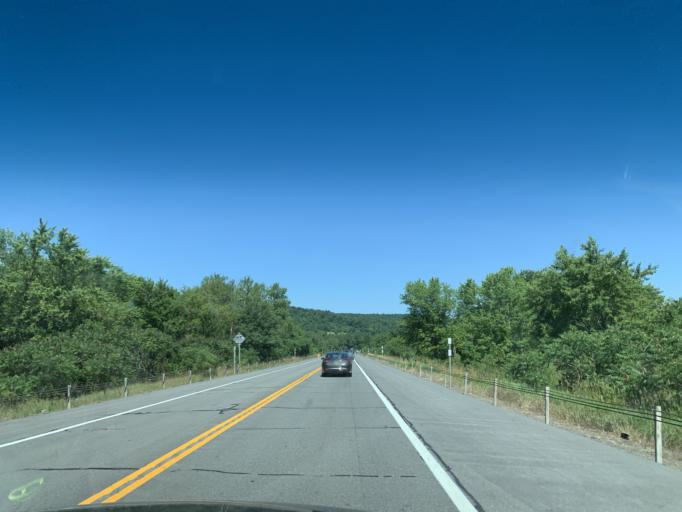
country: US
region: New York
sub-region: Delaware County
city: Sidney
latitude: 42.3111
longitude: -75.4070
